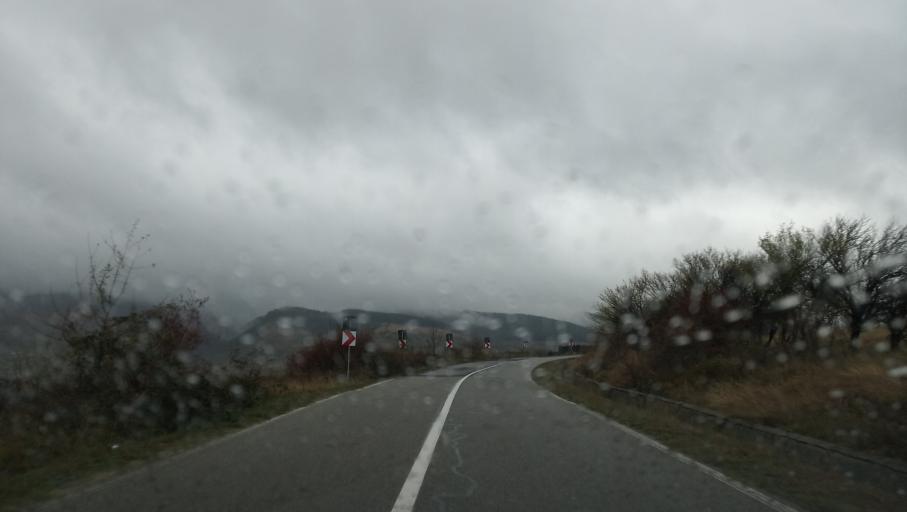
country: RO
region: Gorj
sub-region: Comuna Musetesti
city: Musetesti
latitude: 45.1627
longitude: 23.4717
